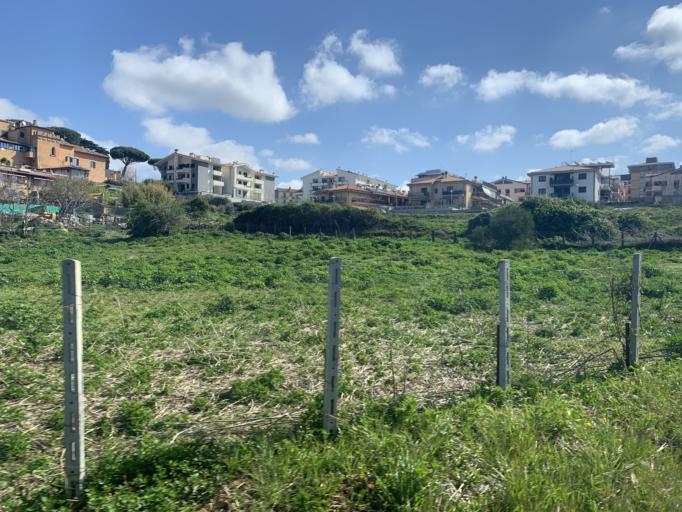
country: IT
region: Latium
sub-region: Citta metropolitana di Roma Capitale
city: Marino
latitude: 41.7701
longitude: 12.6492
